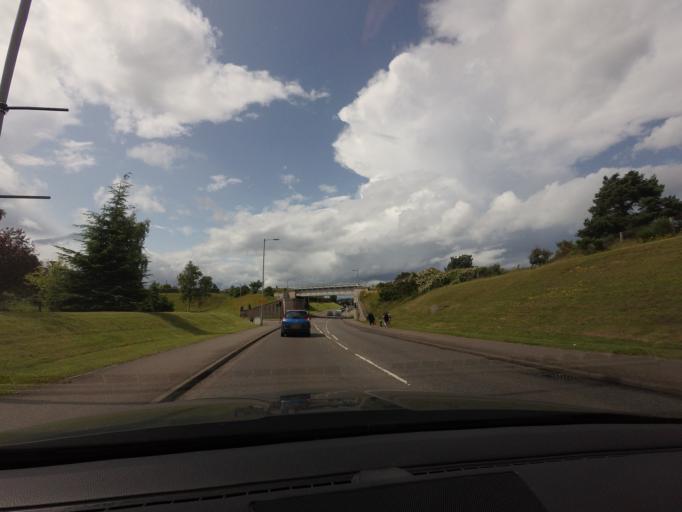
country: GB
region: Scotland
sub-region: Highland
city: Nairn
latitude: 57.5832
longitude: -3.8574
